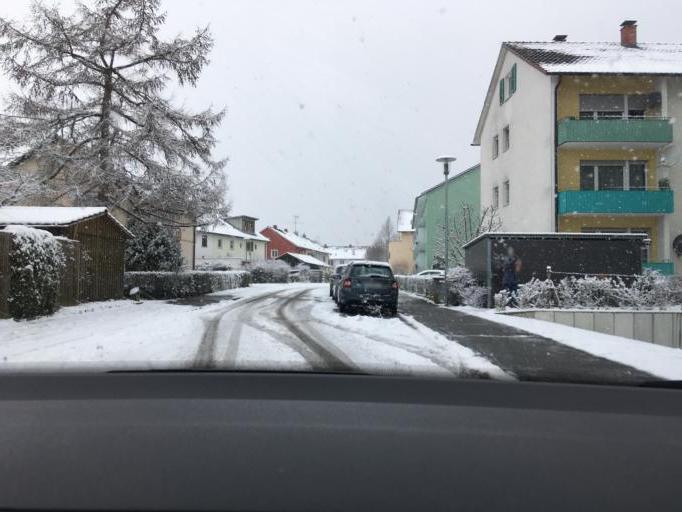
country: DE
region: Baden-Wuerttemberg
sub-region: Freiburg Region
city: Gottmadingen
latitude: 47.7331
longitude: 8.7884
